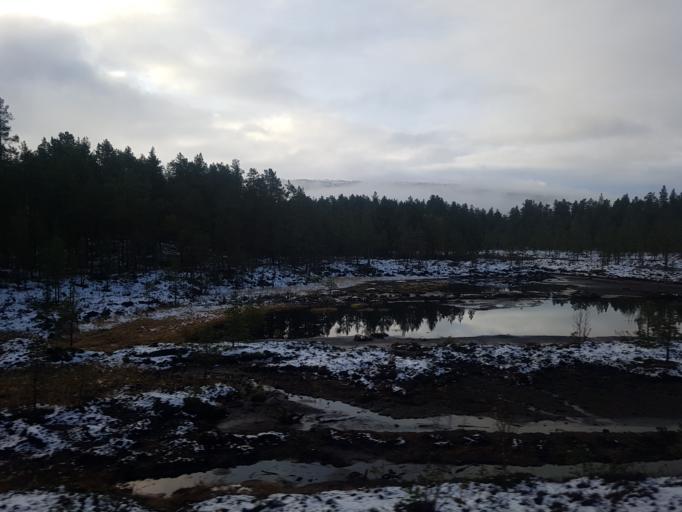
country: NO
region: Sor-Trondelag
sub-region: Oppdal
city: Oppdal
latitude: 62.6292
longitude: 9.7844
